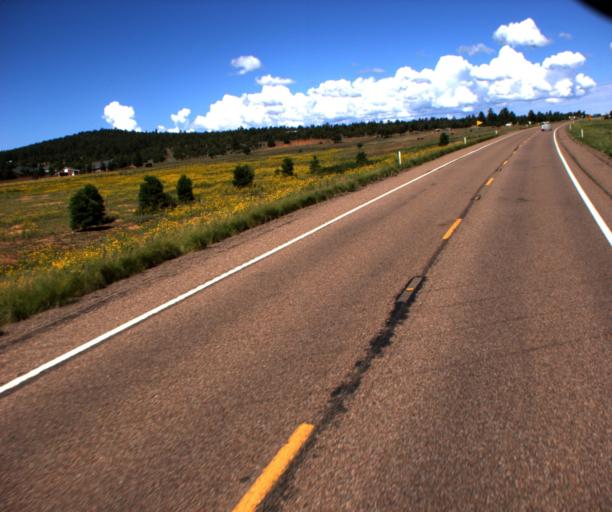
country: US
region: Arizona
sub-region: Navajo County
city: Linden
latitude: 34.3153
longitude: -110.2433
